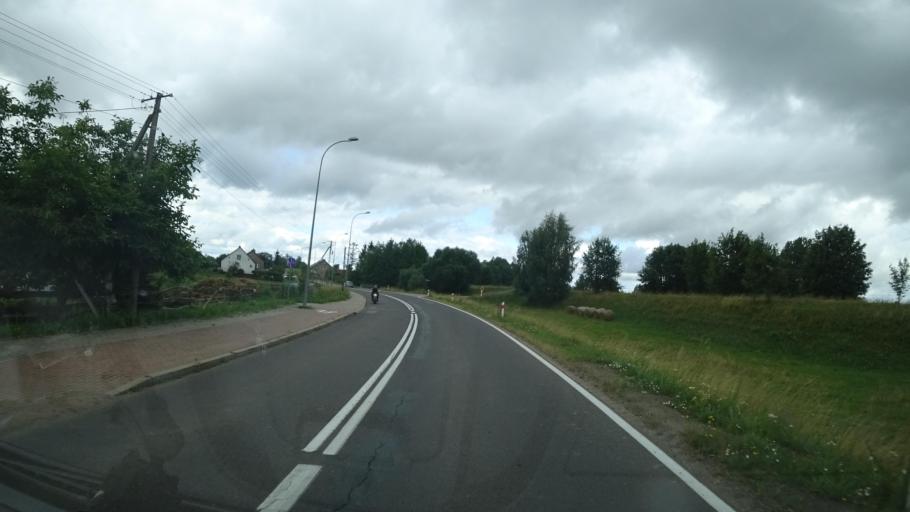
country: PL
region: Warmian-Masurian Voivodeship
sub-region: Powiat olecki
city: Kowale Oleckie
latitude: 54.1775
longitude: 22.4148
